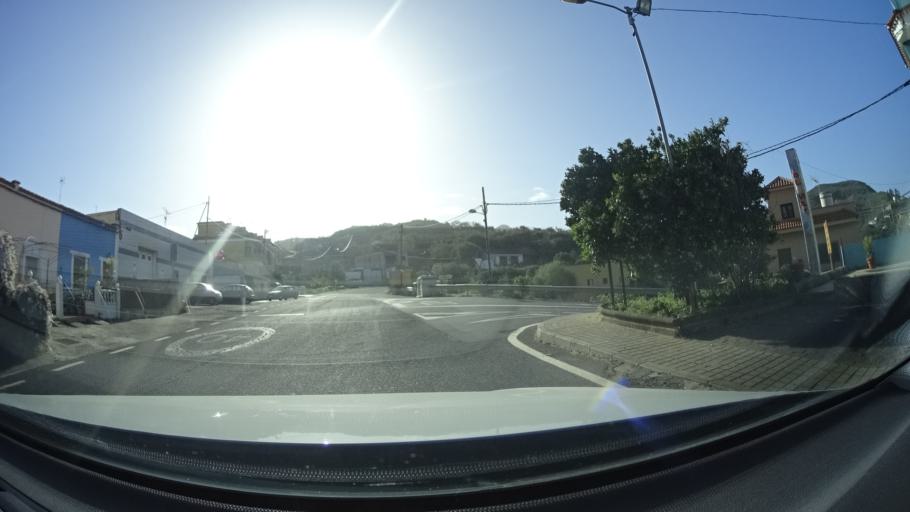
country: ES
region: Canary Islands
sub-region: Provincia de Las Palmas
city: Vega de San Mateo
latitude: 28.0257
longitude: -15.5454
